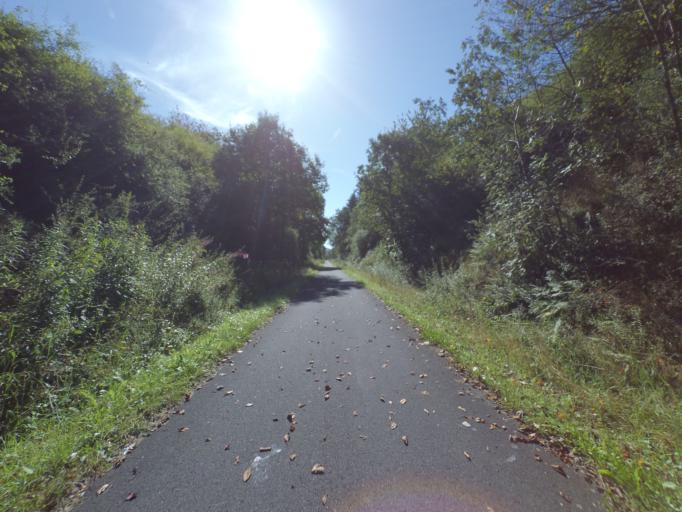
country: DE
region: Rheinland-Pfalz
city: Schalkenmehren
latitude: 50.1644
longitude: 6.8693
